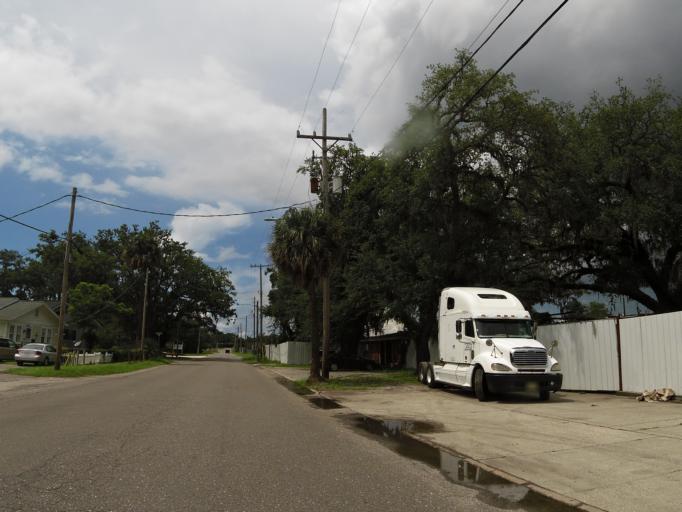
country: US
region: Florida
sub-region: Duval County
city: Jacksonville
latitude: 30.3742
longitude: -81.6403
